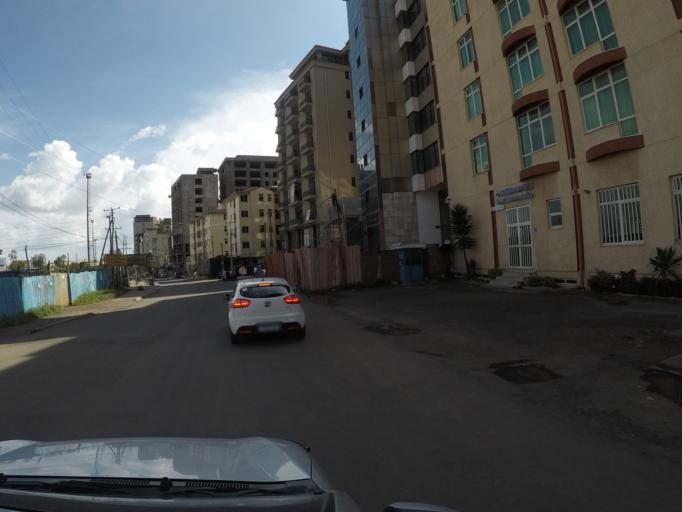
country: ET
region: Adis Abeba
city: Addis Ababa
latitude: 8.9928
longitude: 38.7888
